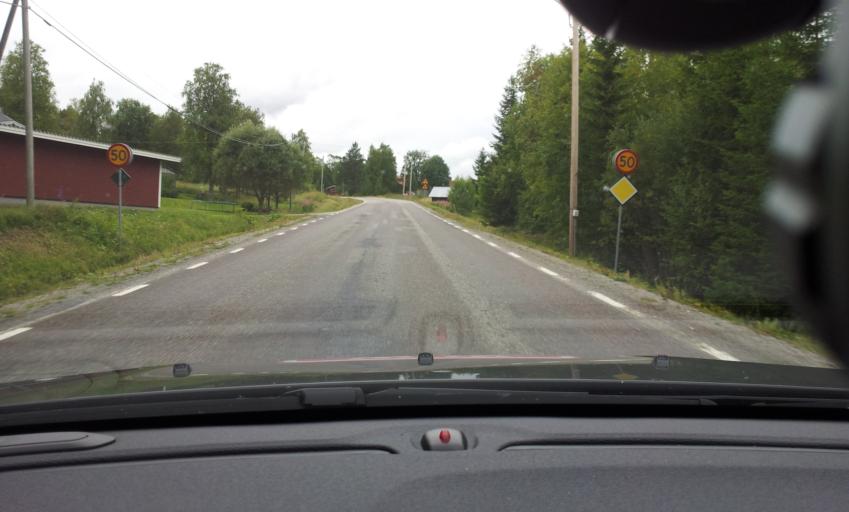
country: SE
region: Jaemtland
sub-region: Braecke Kommun
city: Braecke
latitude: 62.9728
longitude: 15.1741
